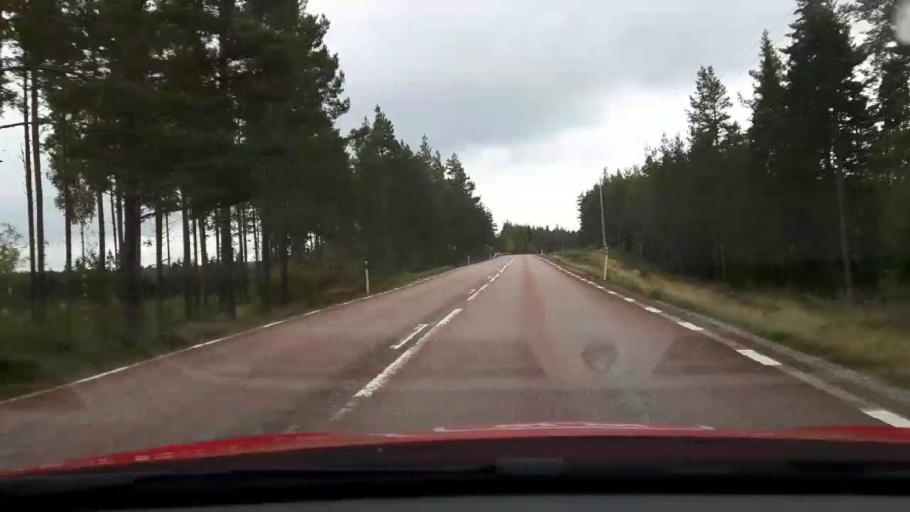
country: SE
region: Gaevleborg
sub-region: Soderhamns Kommun
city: Soderhamn
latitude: 61.1260
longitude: 16.9310
